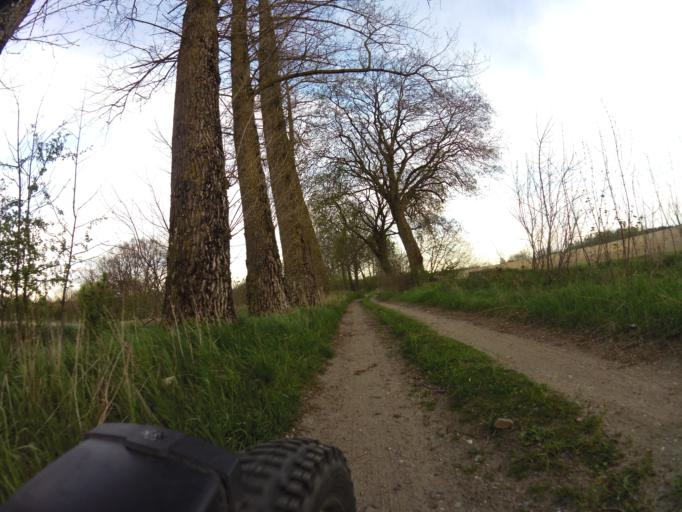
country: PL
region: West Pomeranian Voivodeship
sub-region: Powiat lobeski
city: Lobez
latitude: 53.7231
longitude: 15.6423
